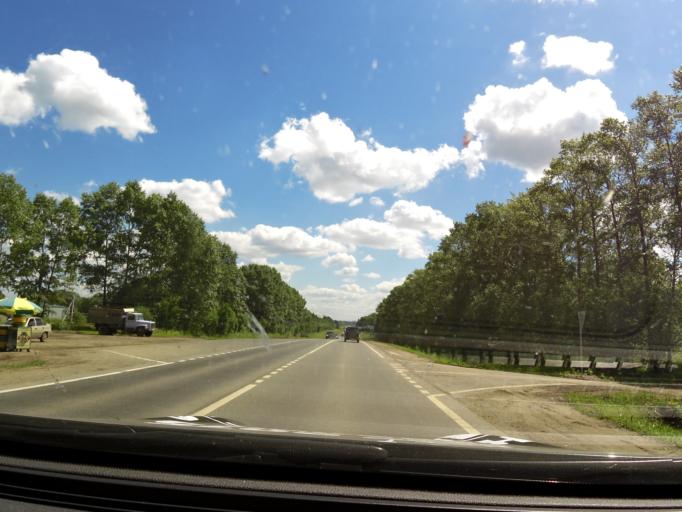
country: RU
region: Vologda
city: Molochnoye
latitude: 59.2590
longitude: 39.7517
